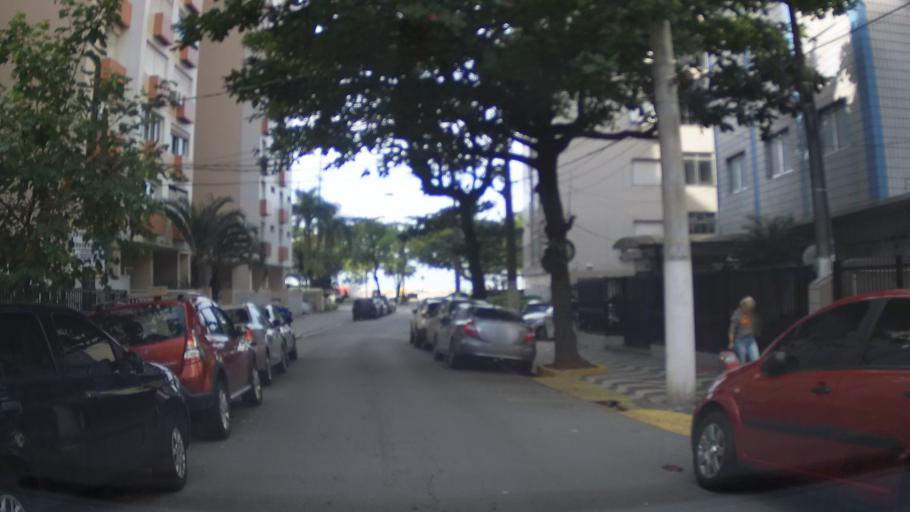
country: BR
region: Sao Paulo
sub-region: Santos
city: Santos
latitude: -23.9695
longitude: -46.3303
